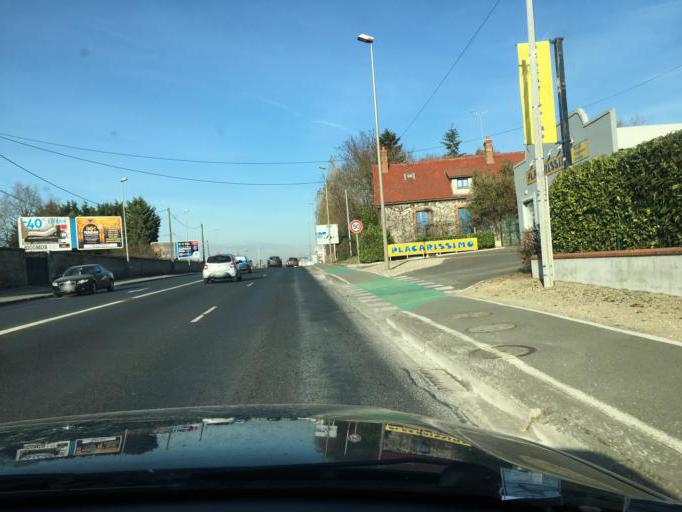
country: FR
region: Centre
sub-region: Departement du Loiret
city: Saran
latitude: 47.9552
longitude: 1.8911
